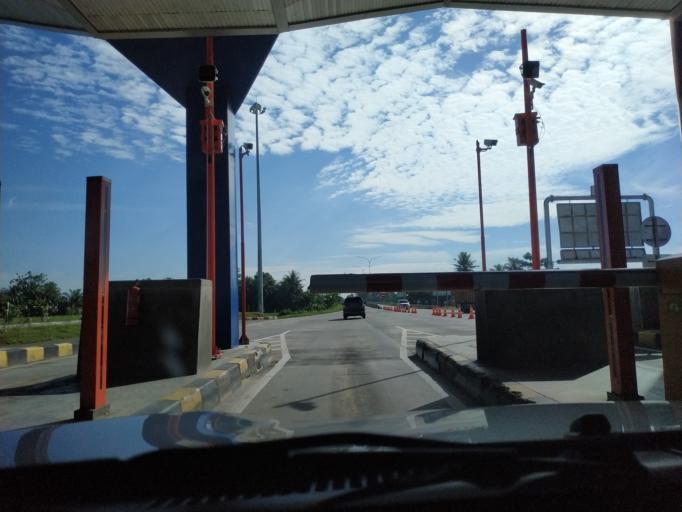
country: ID
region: North Sumatra
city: Tebingtinggi
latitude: 3.4574
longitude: 99.1400
